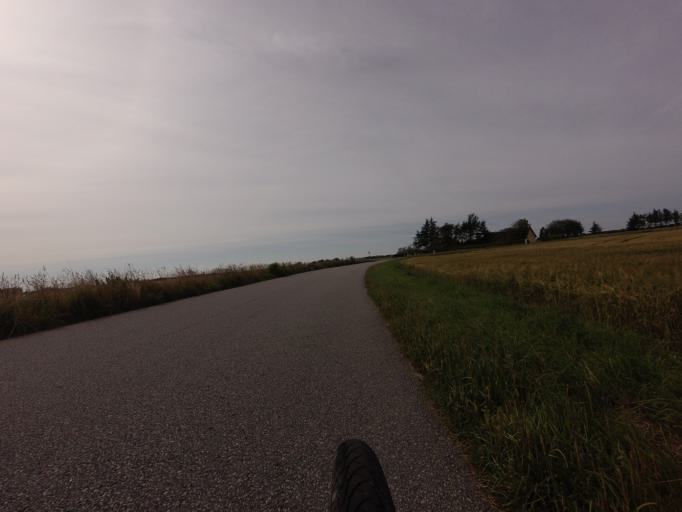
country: DK
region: North Denmark
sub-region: Hjorring Kommune
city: Hjorring
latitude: 57.4355
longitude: 9.8716
